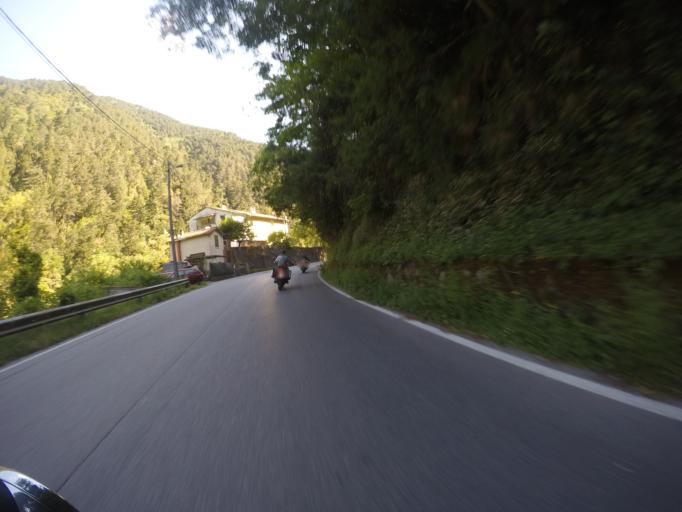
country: IT
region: Tuscany
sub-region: Provincia di Massa-Carrara
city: Montignoso
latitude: 44.0473
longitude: 10.1552
